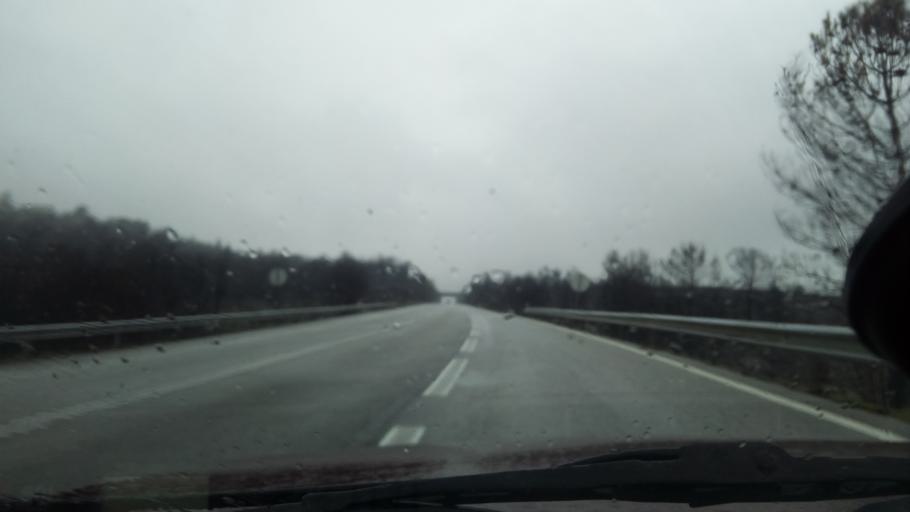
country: PT
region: Guarda
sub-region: Fornos de Algodres
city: Fornos de Algodres
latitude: 40.6144
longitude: -7.5986
